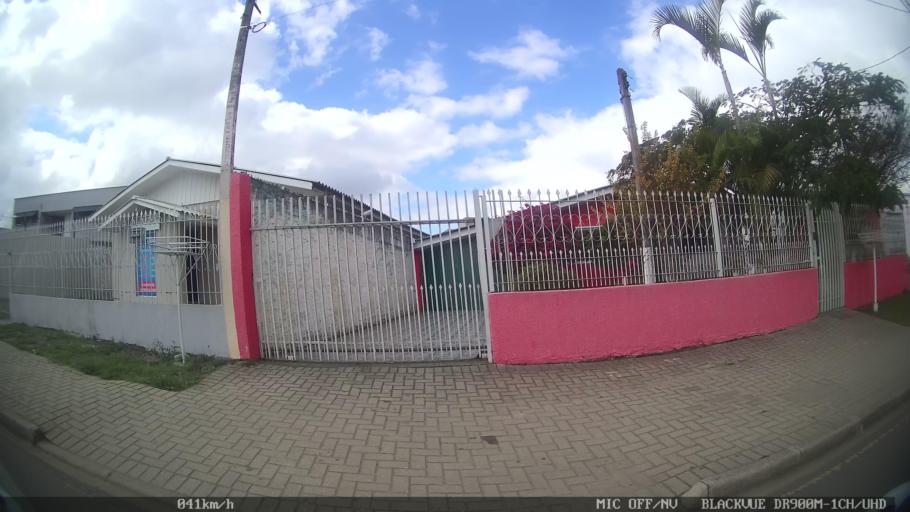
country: BR
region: Parana
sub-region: Pinhais
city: Pinhais
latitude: -25.3729
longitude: -49.2002
